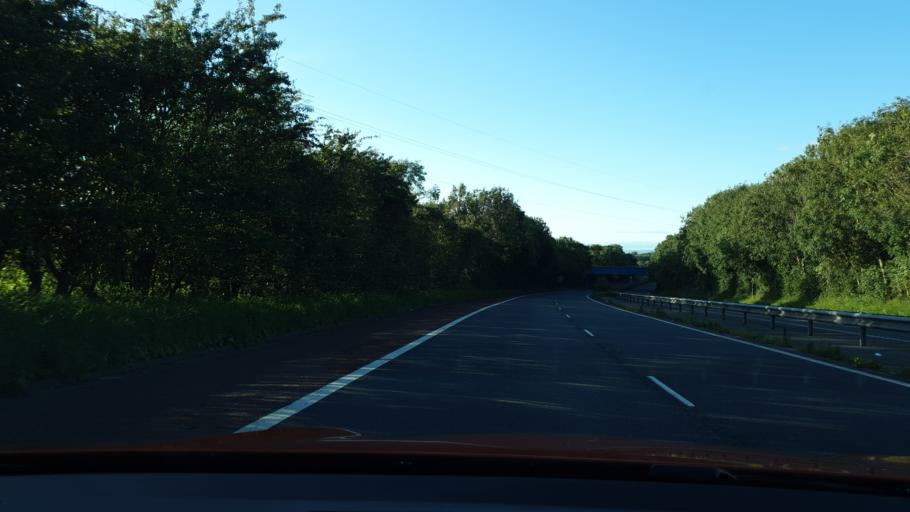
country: GB
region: England
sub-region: Lancashire
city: Carnforth
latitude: 54.1308
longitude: -2.7516
